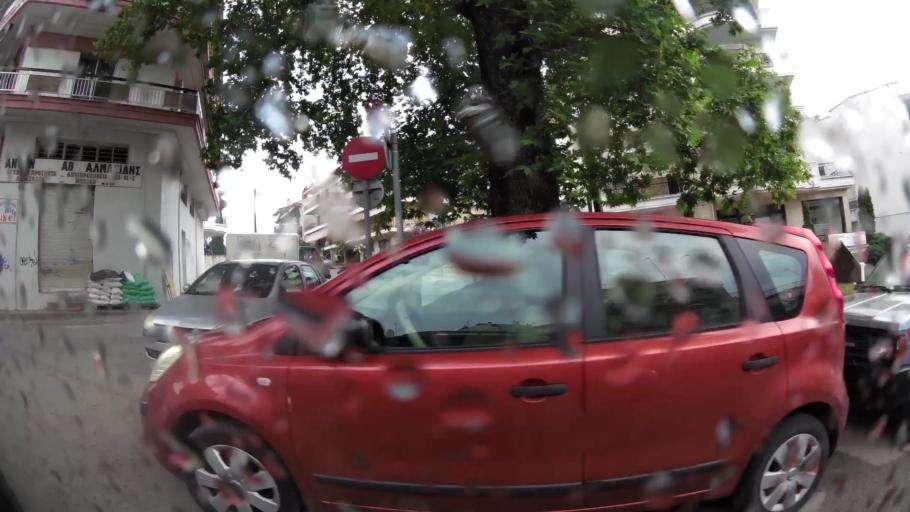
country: GR
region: Central Macedonia
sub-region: Nomos Imathias
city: Veroia
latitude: 40.5293
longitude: 22.2008
